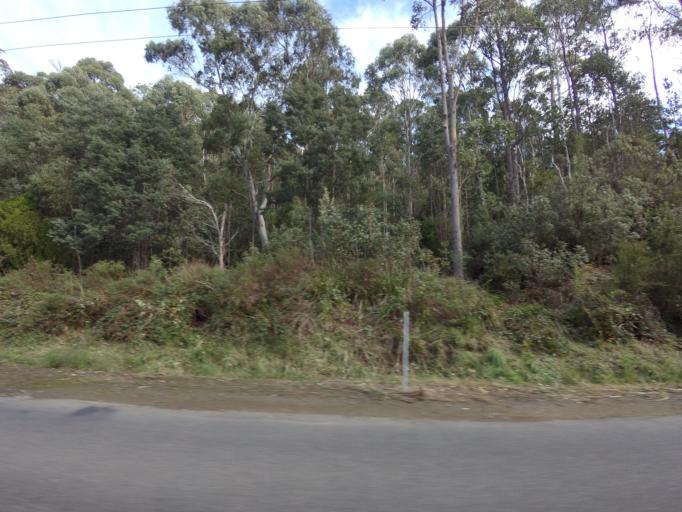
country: AU
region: Tasmania
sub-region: Clarence
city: Sandford
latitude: -43.1167
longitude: 147.7550
